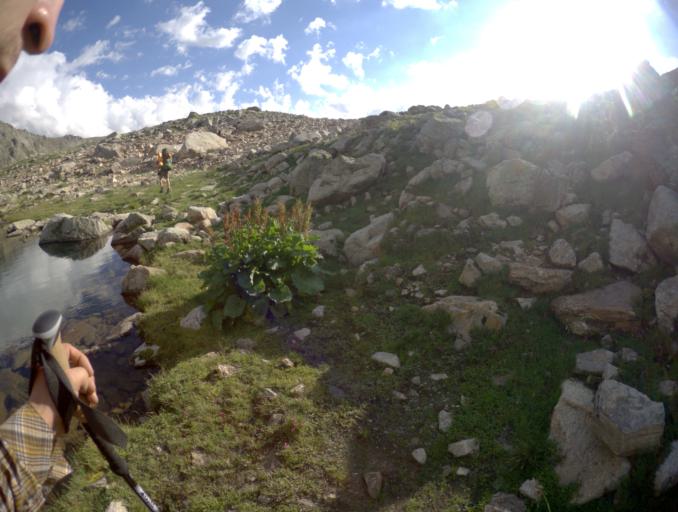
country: RU
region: Karachayevo-Cherkesiya
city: Uchkulan
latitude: 43.3139
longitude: 42.0672
